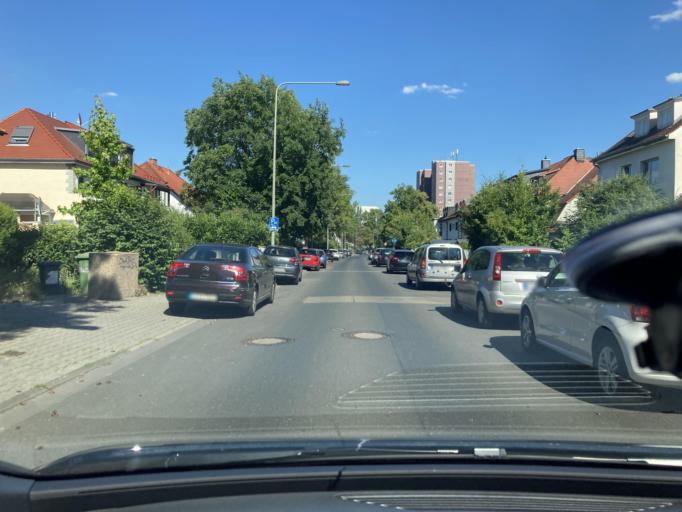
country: DE
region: Hesse
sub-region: Regierungsbezirk Darmstadt
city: Steinbach am Taunus
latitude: 50.1634
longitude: 8.6247
